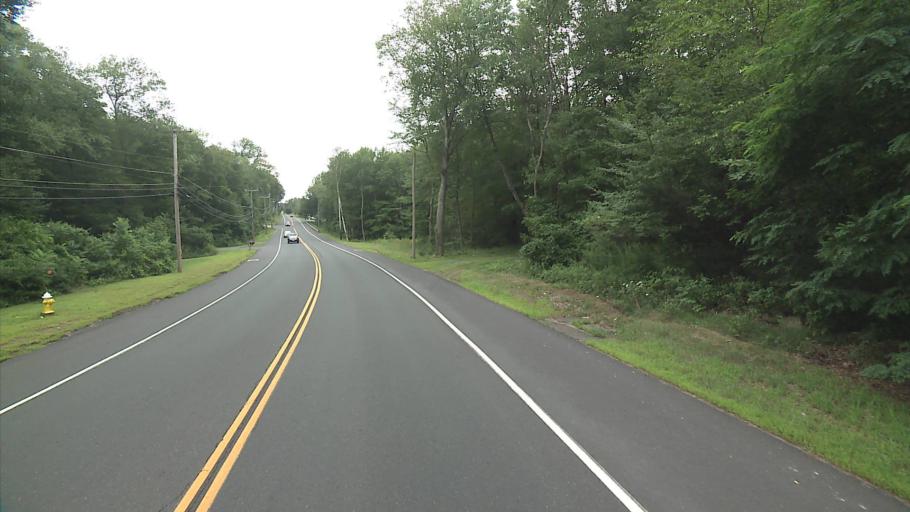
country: US
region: Connecticut
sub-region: Tolland County
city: Tolland
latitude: 41.8769
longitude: -72.3791
